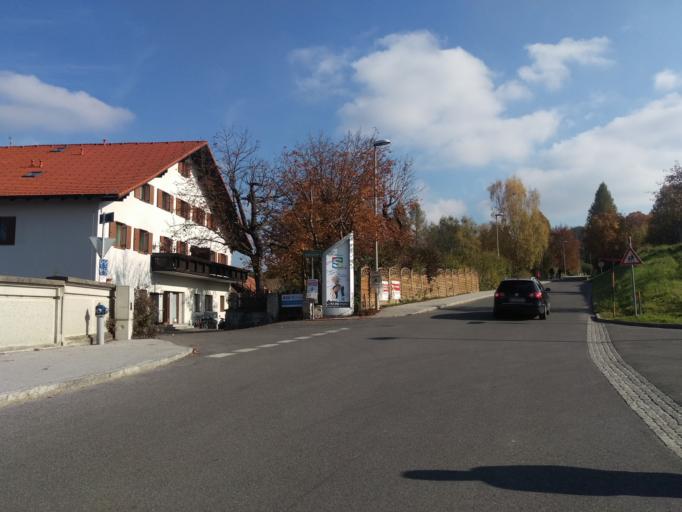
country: AT
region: Styria
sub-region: Graz Stadt
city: Mariatrost
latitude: 47.1066
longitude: 15.4933
